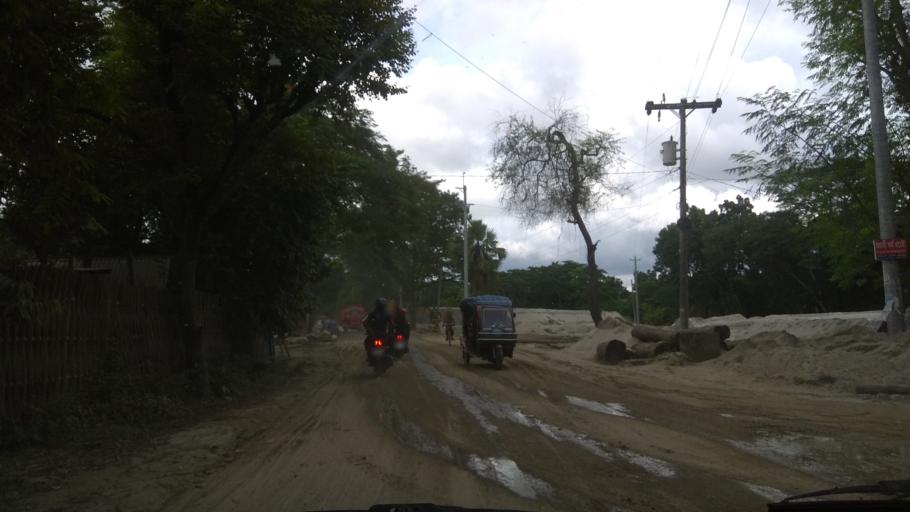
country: BD
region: Khulna
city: Kalia
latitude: 23.1964
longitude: 89.6964
